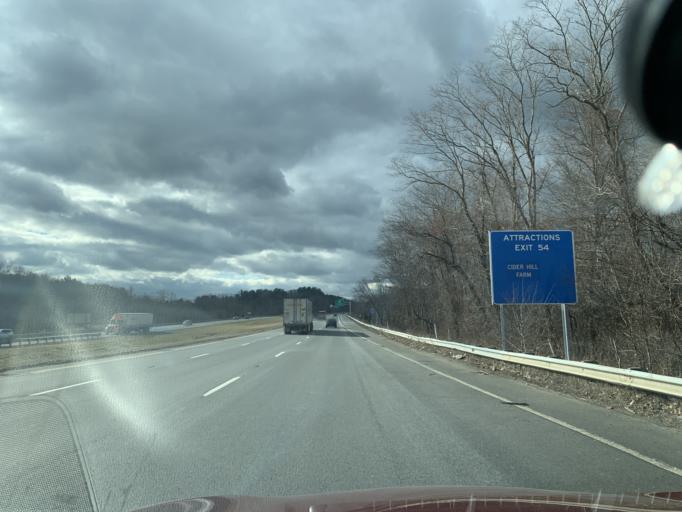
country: US
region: Massachusetts
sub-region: Essex County
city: Amesbury
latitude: 42.8457
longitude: -70.9217
